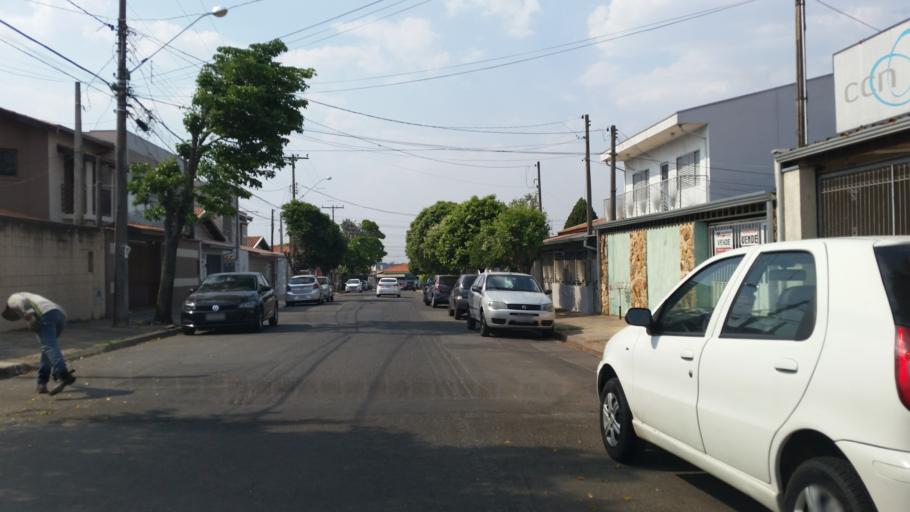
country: BR
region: Sao Paulo
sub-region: Hortolandia
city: Hortolandia
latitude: -22.8851
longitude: -47.1965
